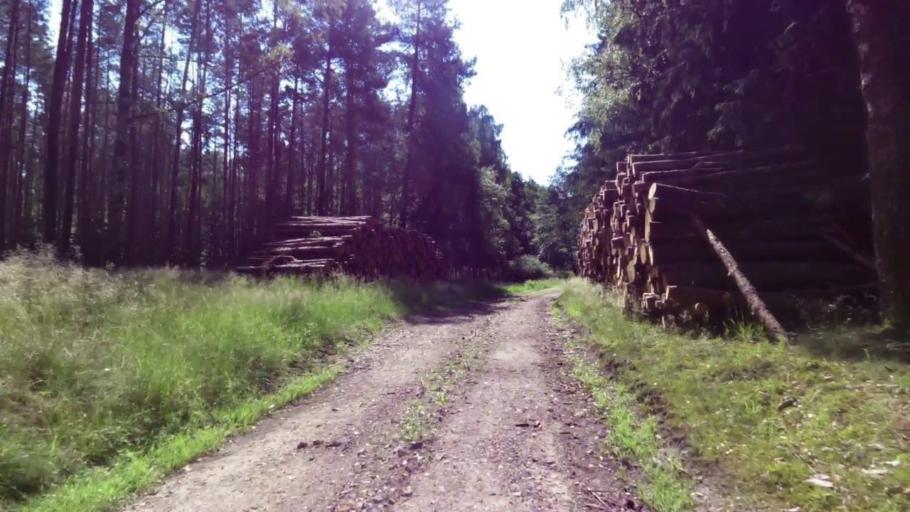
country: PL
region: West Pomeranian Voivodeship
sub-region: Powiat swidwinski
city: Polczyn-Zdroj
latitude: 53.8774
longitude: 16.1015
